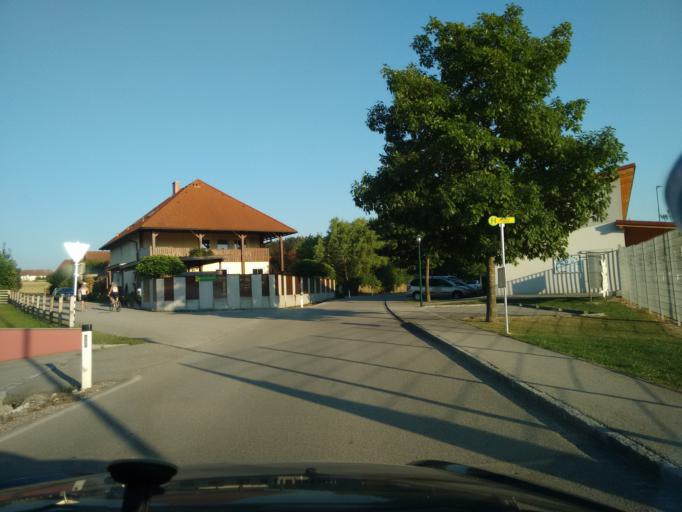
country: AT
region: Upper Austria
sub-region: Politischer Bezirk Grieskirchen
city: Bad Schallerbach
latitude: 48.2045
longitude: 13.9587
